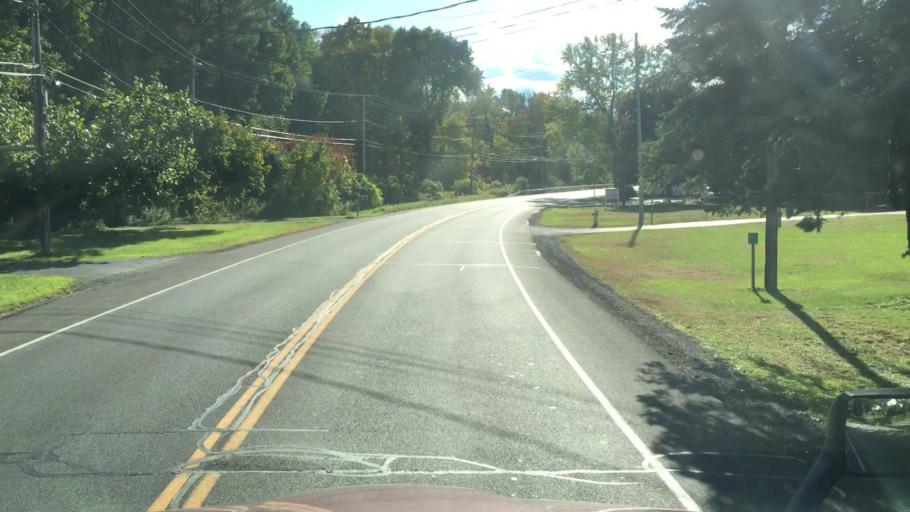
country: US
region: New York
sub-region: Schenectady County
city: Scotia
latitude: 42.8458
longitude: -73.9449
